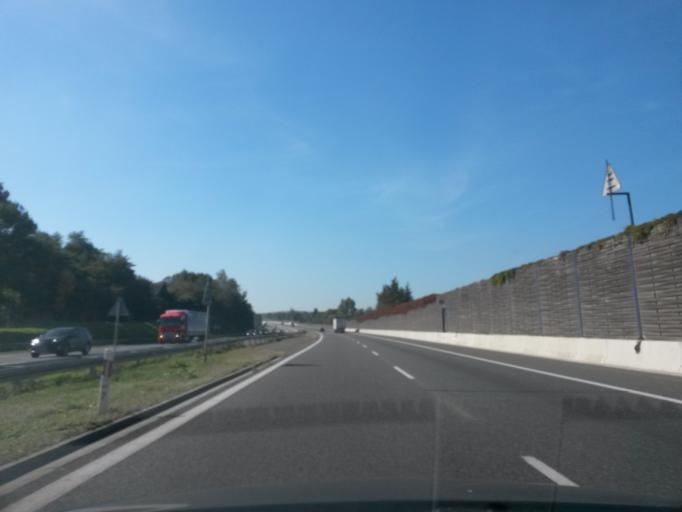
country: PL
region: Lesser Poland Voivodeship
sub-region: Powiat krakowski
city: Mnikow
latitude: 50.0798
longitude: 19.7544
